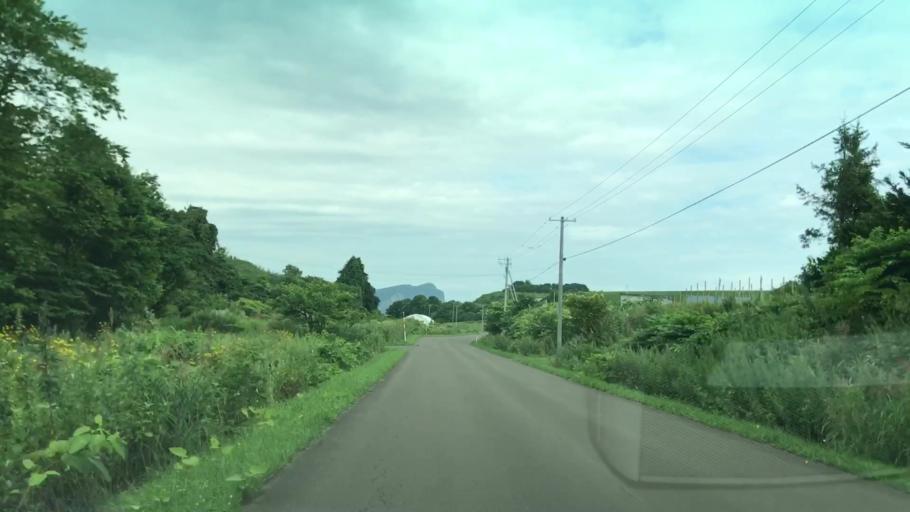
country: JP
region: Hokkaido
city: Yoichi
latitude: 43.1740
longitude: 140.8277
